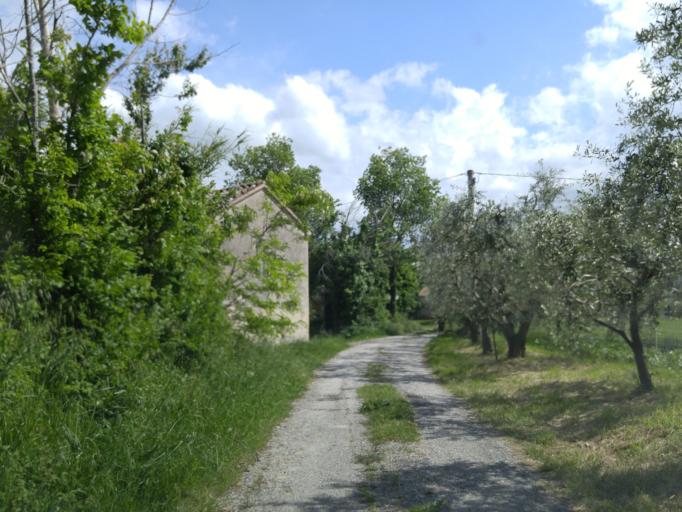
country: IT
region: The Marches
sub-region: Provincia di Pesaro e Urbino
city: Calcinelli
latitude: 43.7661
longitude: 12.9130
